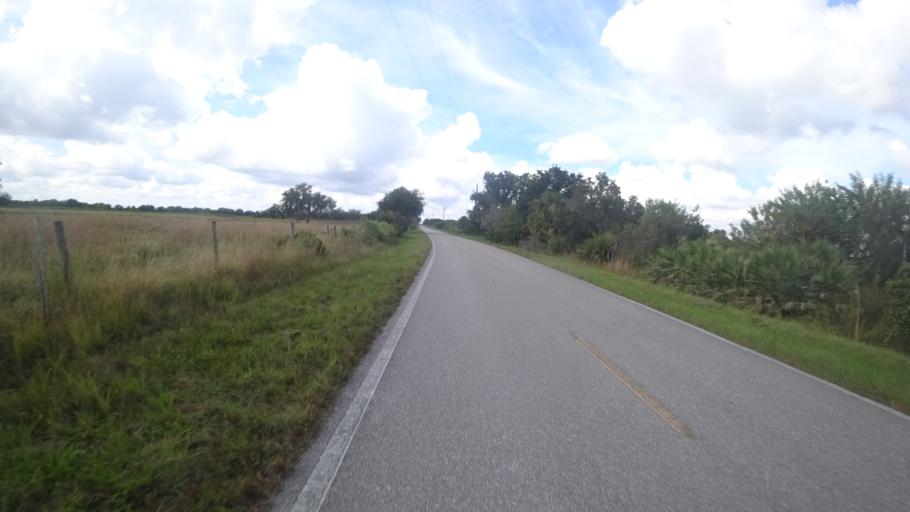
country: US
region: Florida
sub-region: Hillsborough County
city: Wimauma
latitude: 27.6081
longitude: -82.2209
